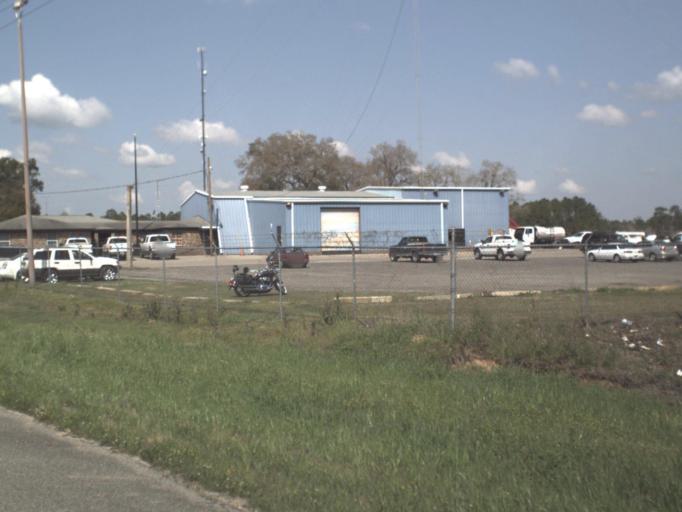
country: US
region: Florida
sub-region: Liberty County
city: Bristol
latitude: 30.3892
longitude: -84.7918
